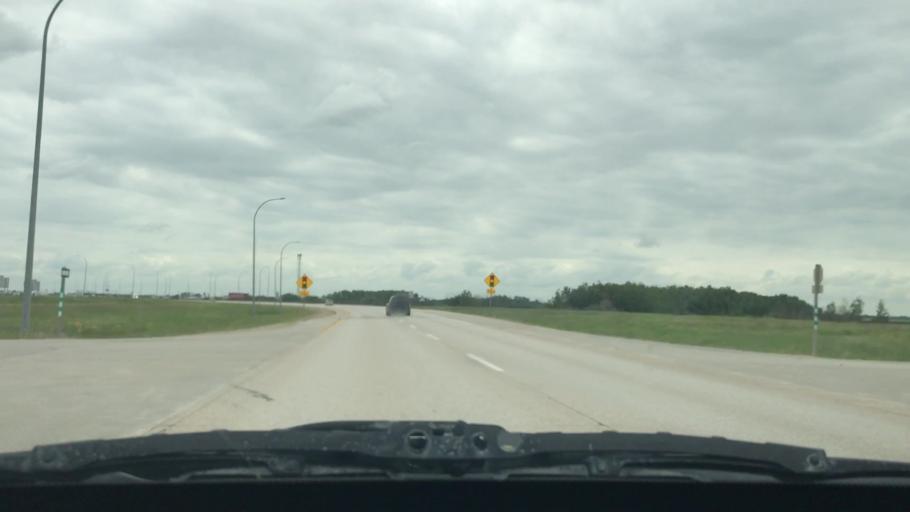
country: CA
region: Manitoba
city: Winnipeg
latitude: 49.8267
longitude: -96.9480
